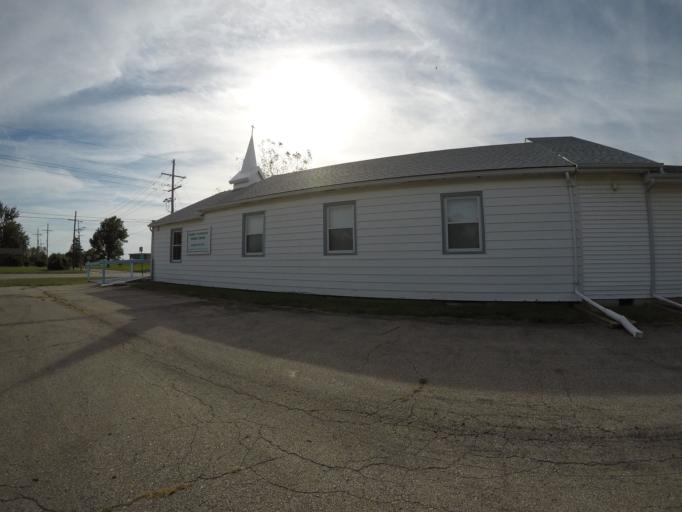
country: US
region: Kansas
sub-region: Johnson County
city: Gardner
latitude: 38.8114
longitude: -94.9363
